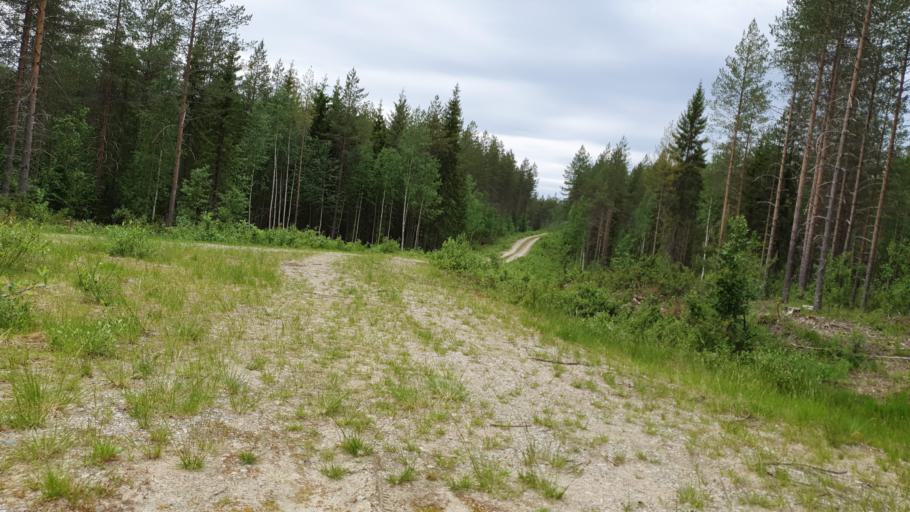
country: FI
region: Kainuu
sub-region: Kehys-Kainuu
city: Kuhmo
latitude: 64.4473
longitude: 29.7063
